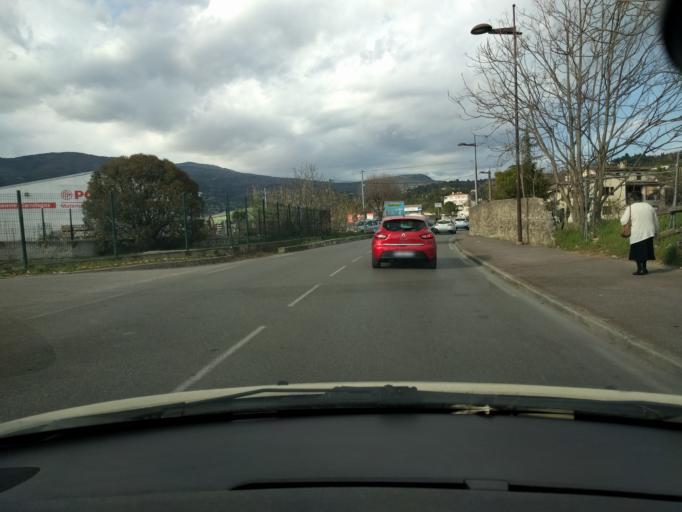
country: FR
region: Provence-Alpes-Cote d'Azur
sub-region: Departement des Alpes-Maritimes
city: Mouans-Sartoux
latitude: 43.6394
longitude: 6.9561
